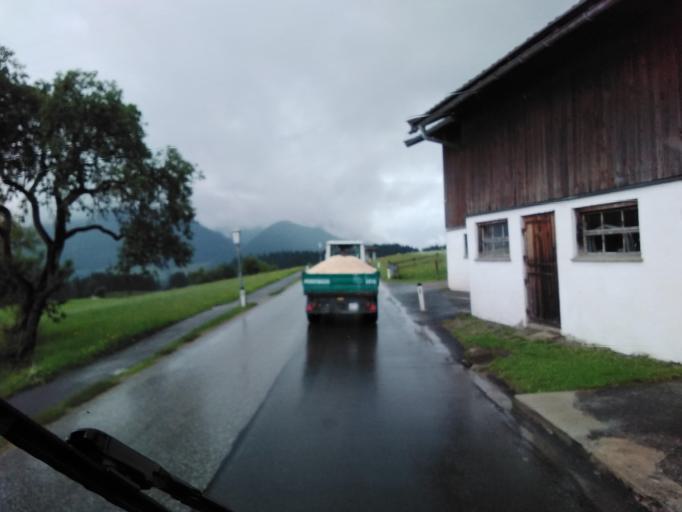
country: AT
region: Tyrol
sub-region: Politischer Bezirk Kitzbuhel
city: Schwendt
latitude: 47.6361
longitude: 12.3922
